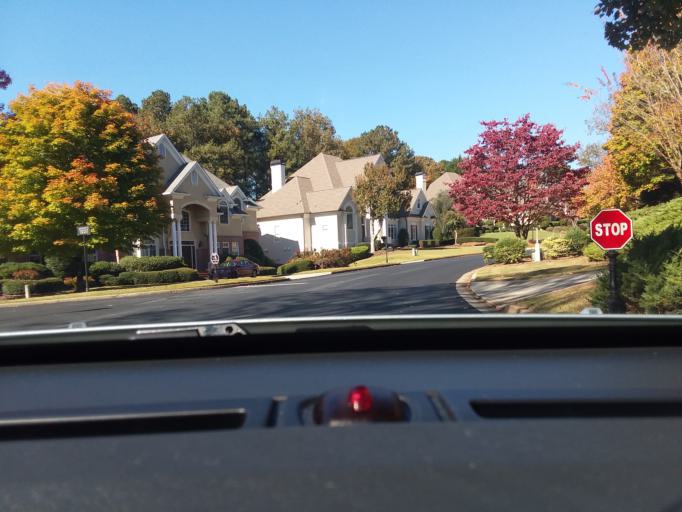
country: US
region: Georgia
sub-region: Fulton County
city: Johns Creek
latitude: 34.0314
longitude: -84.1814
